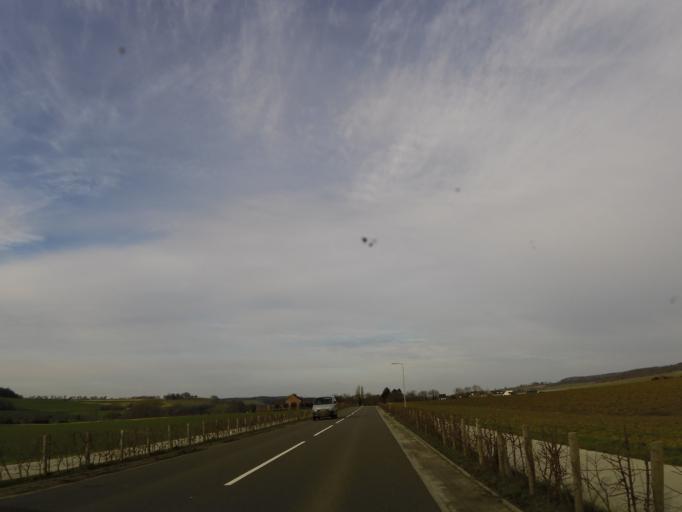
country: NL
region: Limburg
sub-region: Gemeente Voerendaal
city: Ubachsberg
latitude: 50.8038
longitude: 5.9274
